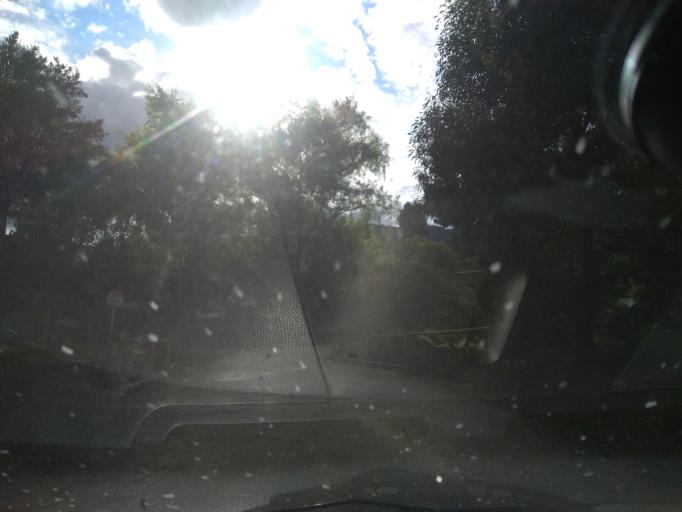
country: CO
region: Boyaca
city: Duitama
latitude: 5.8288
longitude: -73.0803
